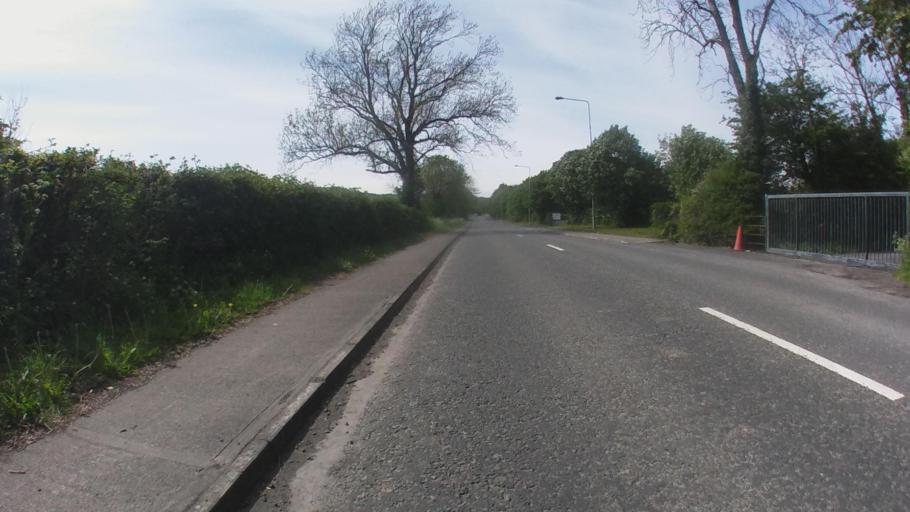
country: IE
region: Leinster
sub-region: County Carlow
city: Carlow
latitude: 52.8401
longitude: -6.9606
